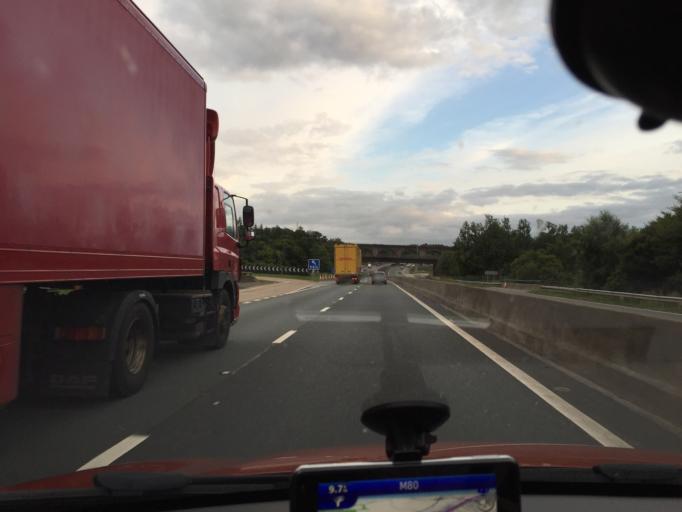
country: GB
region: Scotland
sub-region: Falkirk
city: Dunipace
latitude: 55.9858
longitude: -3.9439
